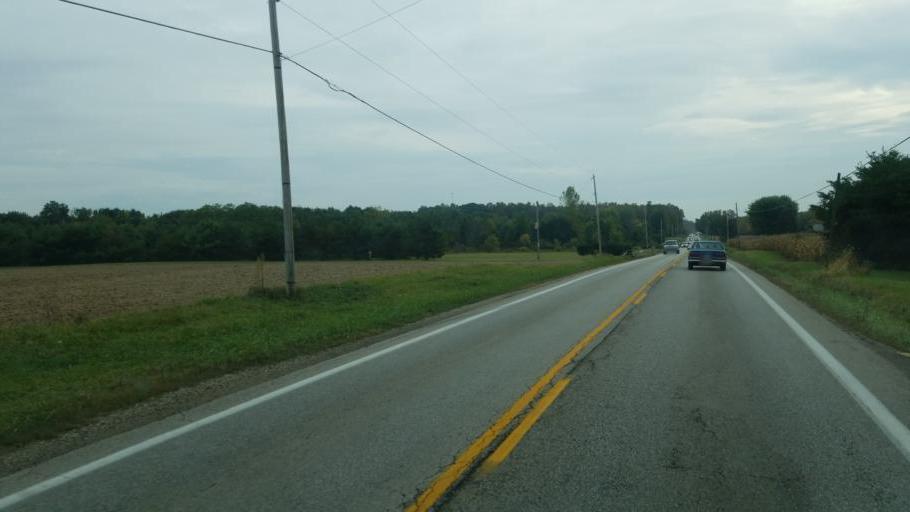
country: US
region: Ohio
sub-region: Morrow County
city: Cardington
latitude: 40.3970
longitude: -82.8272
